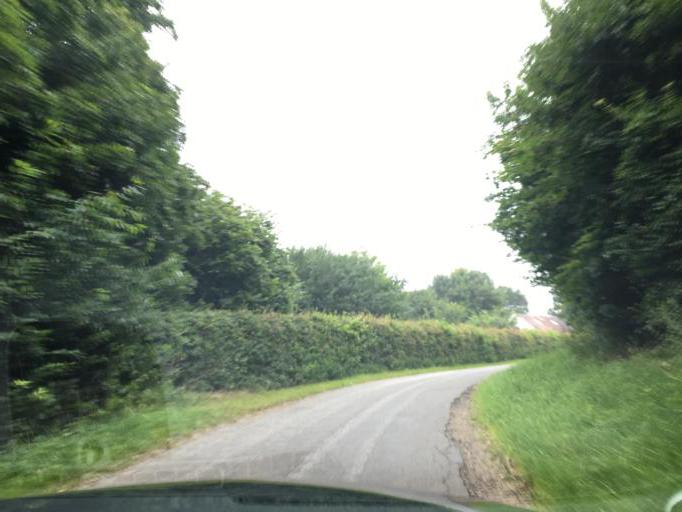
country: DK
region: South Denmark
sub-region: Kolding Kommune
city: Kolding
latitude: 55.5645
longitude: 9.4405
